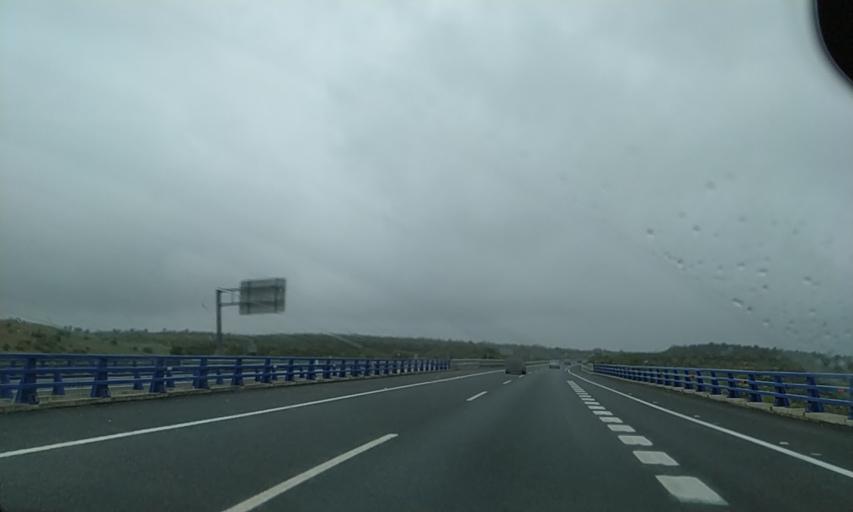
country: ES
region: Extremadura
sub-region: Provincia de Caceres
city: Canaveral
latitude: 39.7944
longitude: -6.3677
